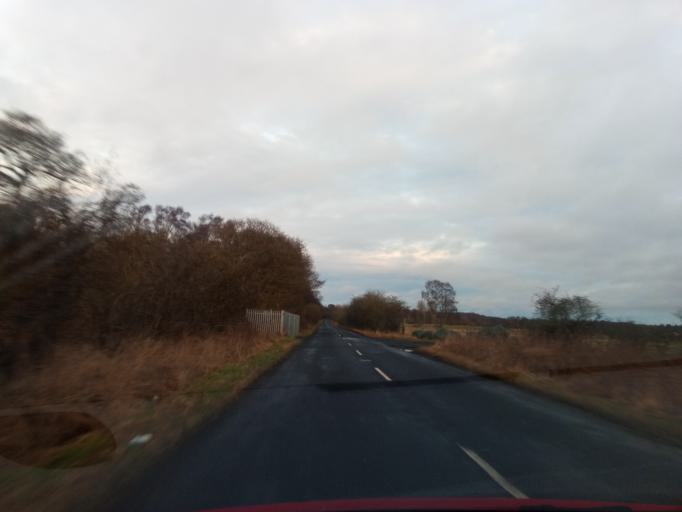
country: GB
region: England
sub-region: Northumberland
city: Meldon
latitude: 55.1317
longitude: -1.7416
